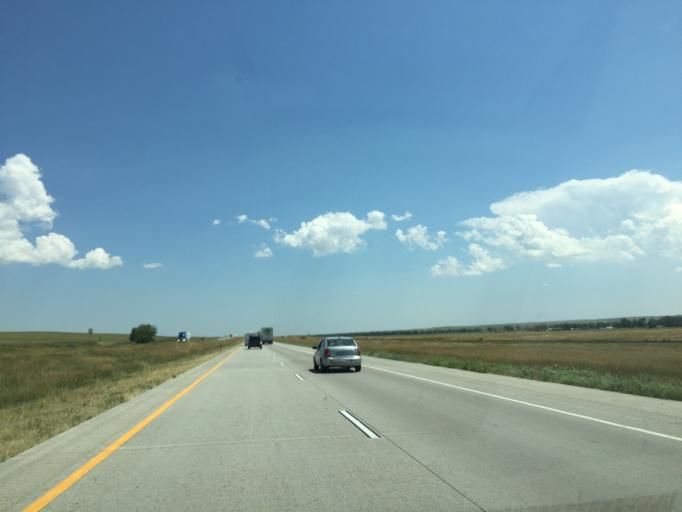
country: US
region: Colorado
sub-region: Lincoln County
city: Limon
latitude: 39.2959
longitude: -103.8036
